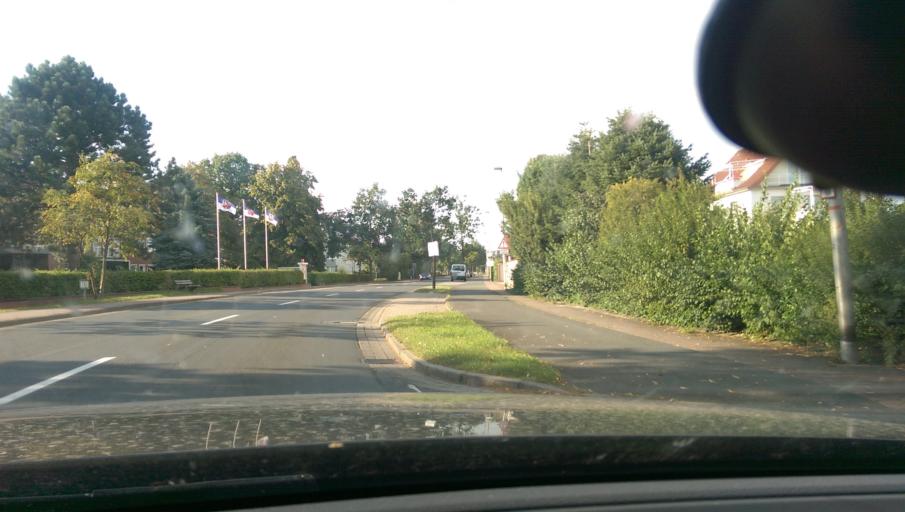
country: DE
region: Lower Saxony
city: Neustadt am Rubenberge
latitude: 52.5098
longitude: 9.4533
